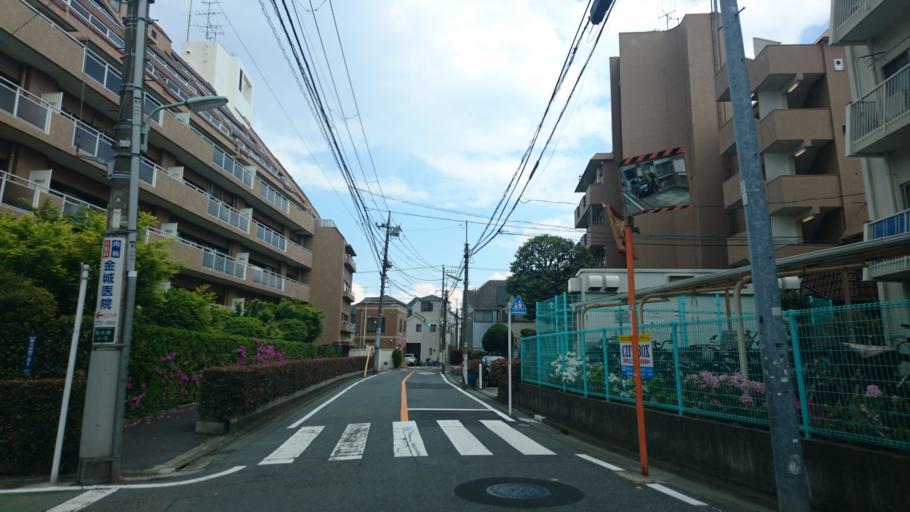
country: JP
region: Kanagawa
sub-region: Kawasaki-shi
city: Kawasaki
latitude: 35.5963
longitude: 139.7213
